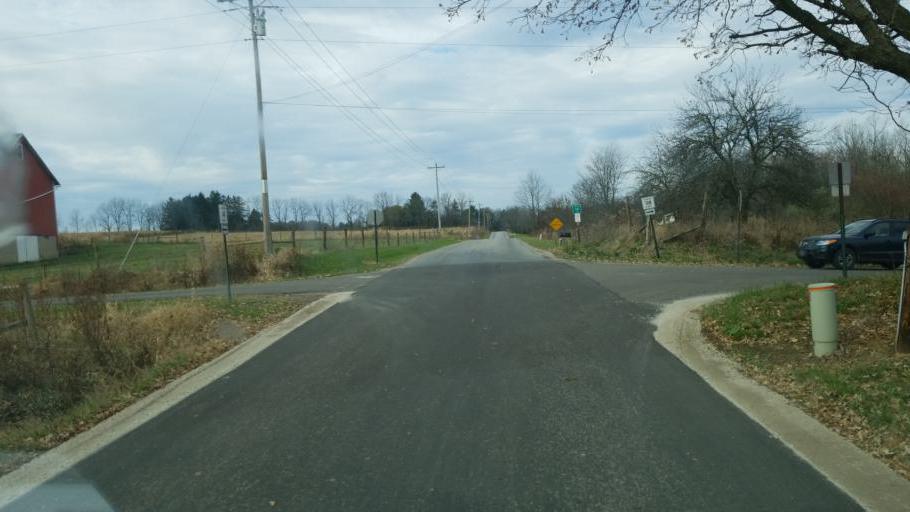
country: US
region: Ohio
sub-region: Morrow County
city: Mount Gilead
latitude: 40.5207
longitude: -82.6880
